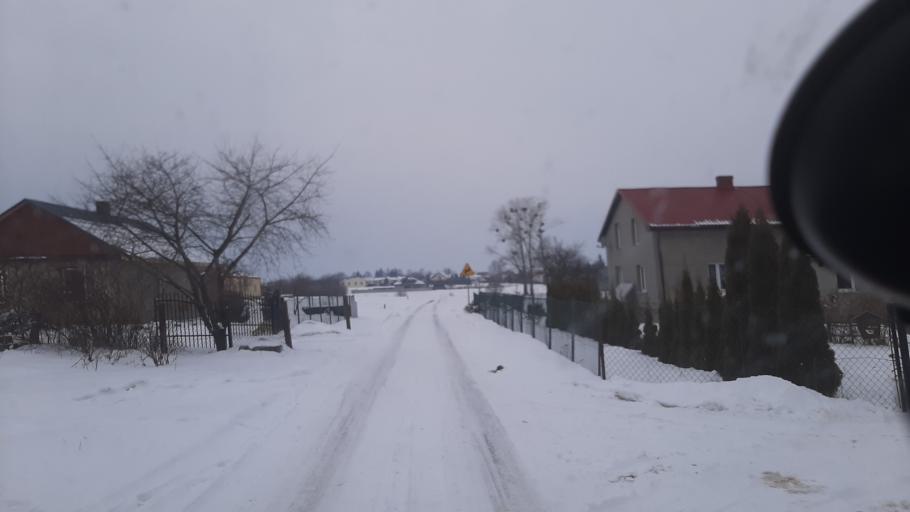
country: PL
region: Lublin Voivodeship
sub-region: Powiat lubelski
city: Garbow
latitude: 51.3564
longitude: 22.3845
